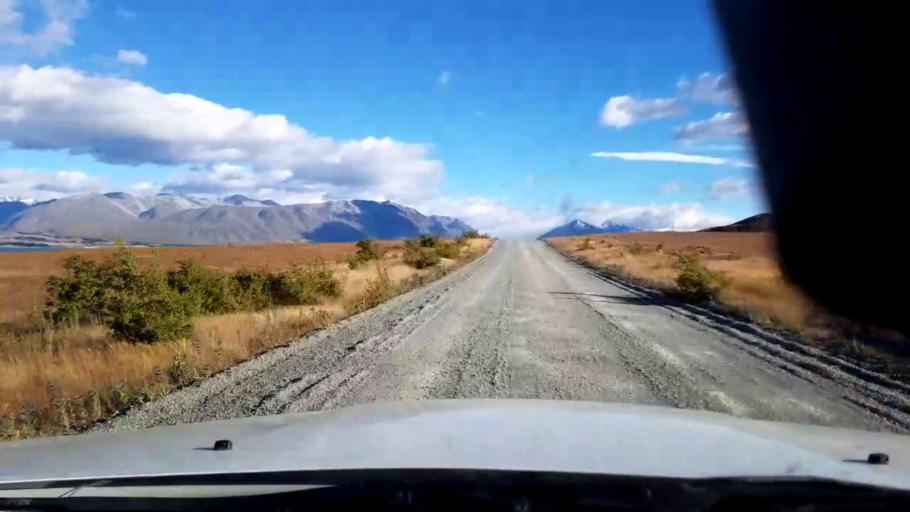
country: NZ
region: Canterbury
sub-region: Timaru District
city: Pleasant Point
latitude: -43.9212
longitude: 170.5592
